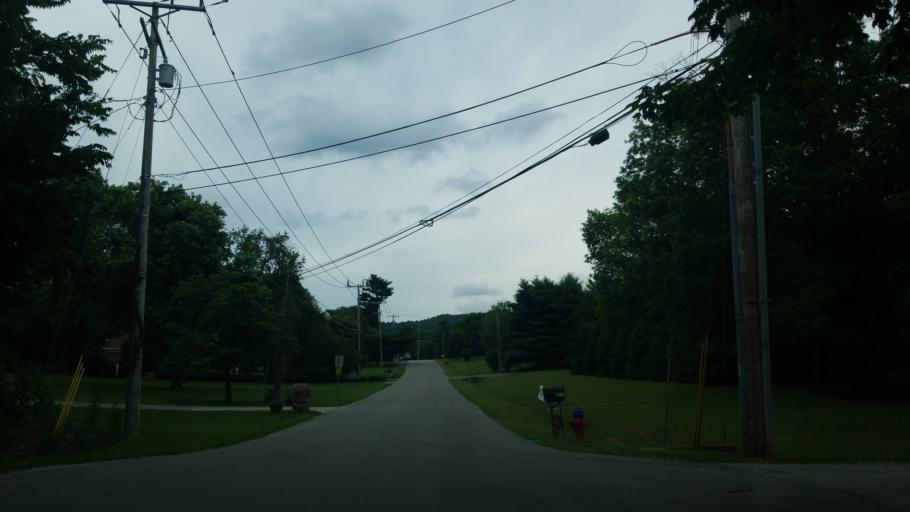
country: US
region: Tennessee
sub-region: Davidson County
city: Forest Hills
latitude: 36.0385
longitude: -86.8208
